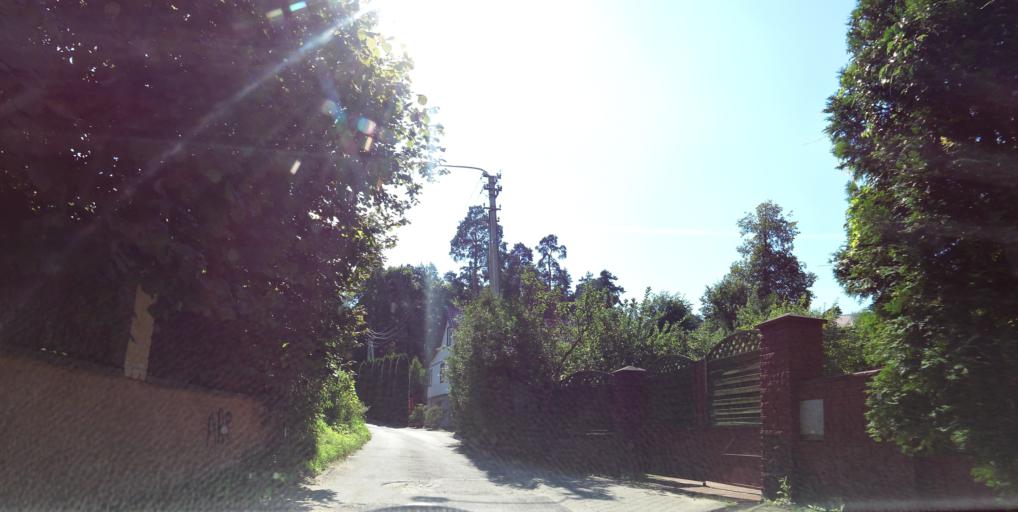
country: LT
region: Vilnius County
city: Rasos
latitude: 54.6922
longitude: 25.3121
